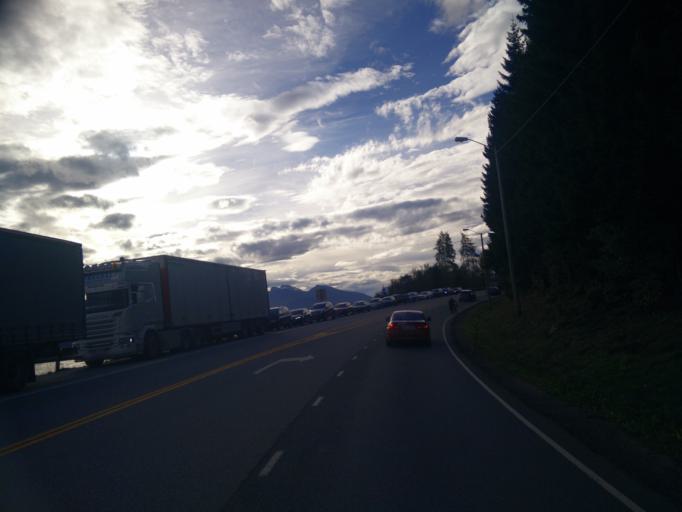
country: NO
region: More og Romsdal
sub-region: Vestnes
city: Vestnes
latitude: 62.6510
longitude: 7.0855
